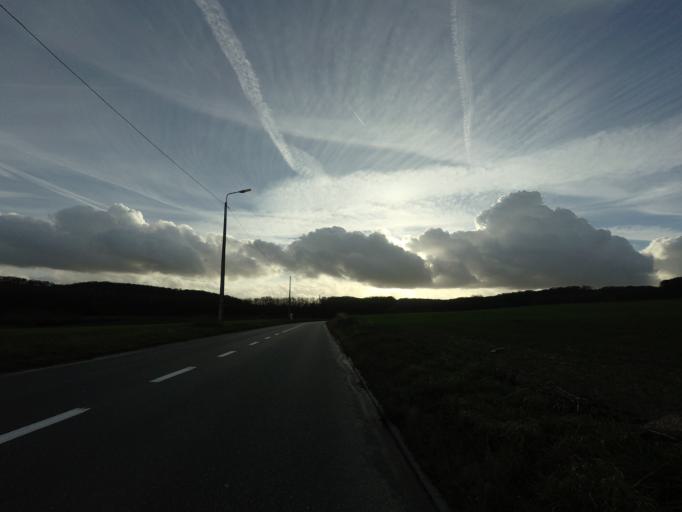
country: BE
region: Flanders
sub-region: Provincie Vlaams-Brabant
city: Kortenberg
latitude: 50.8715
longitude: 4.5648
